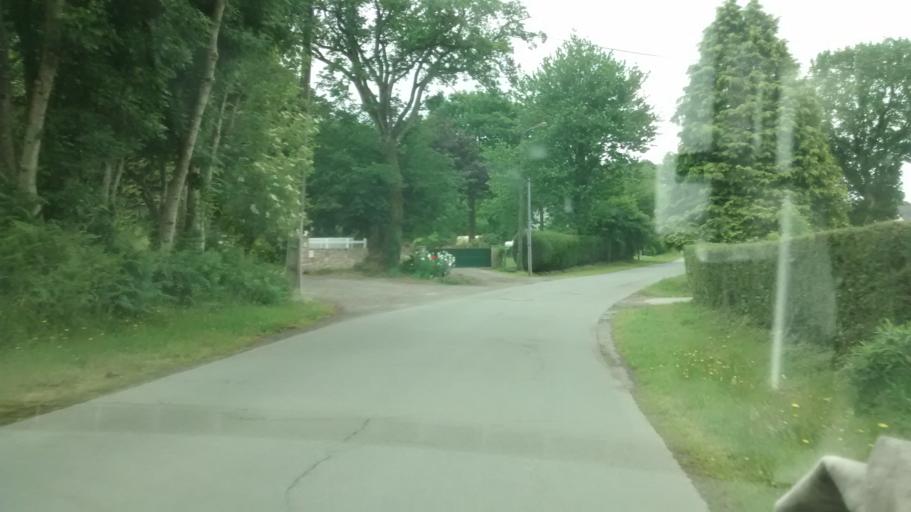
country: FR
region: Brittany
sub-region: Departement du Morbihan
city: Molac
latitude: 47.7287
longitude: -2.4335
